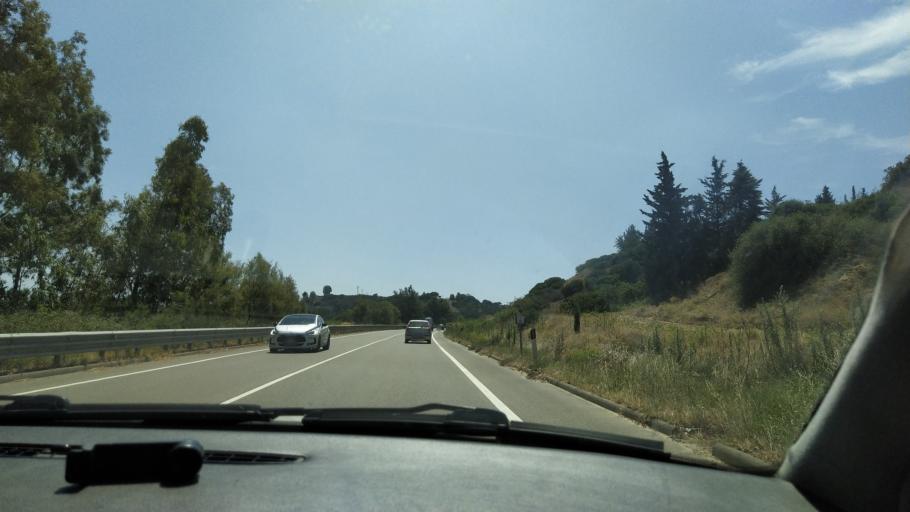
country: IT
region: Apulia
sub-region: Provincia di Taranto
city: Marina di Ginosa
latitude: 40.4324
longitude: 16.7919
